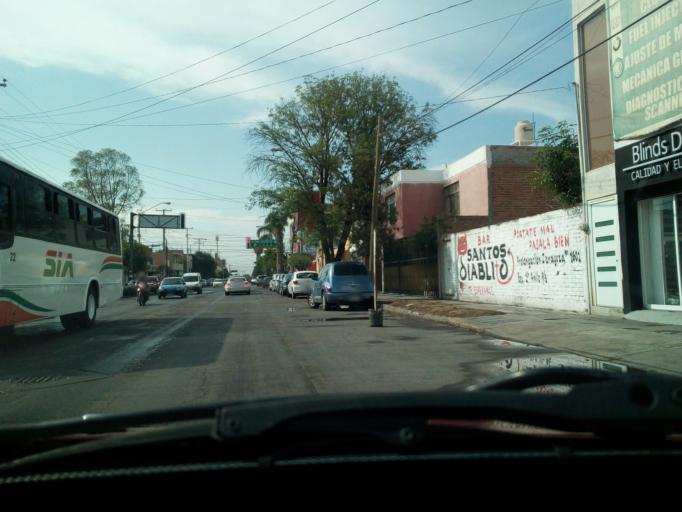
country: MX
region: Aguascalientes
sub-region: Aguascalientes
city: Aguascalientes
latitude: 21.9001
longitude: -102.2989
